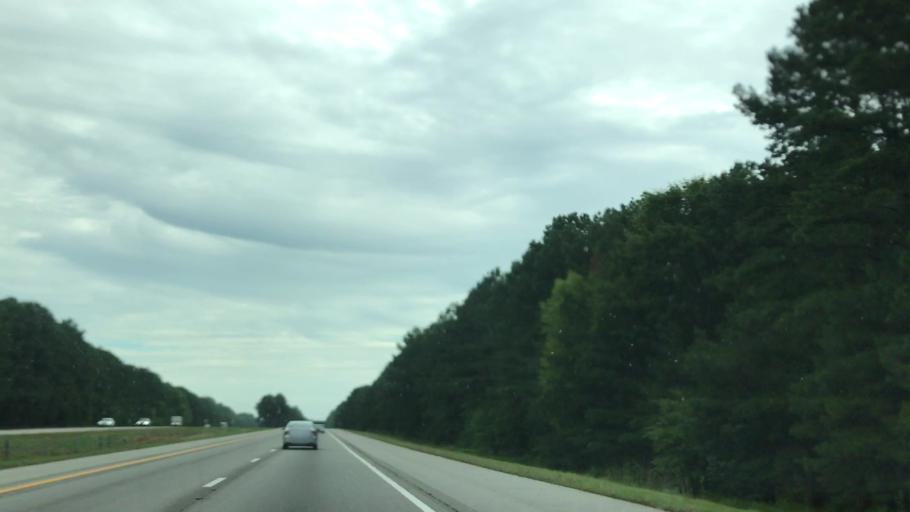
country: US
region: North Carolina
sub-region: Johnston County
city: Kenly
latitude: 35.6424
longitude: -78.0992
